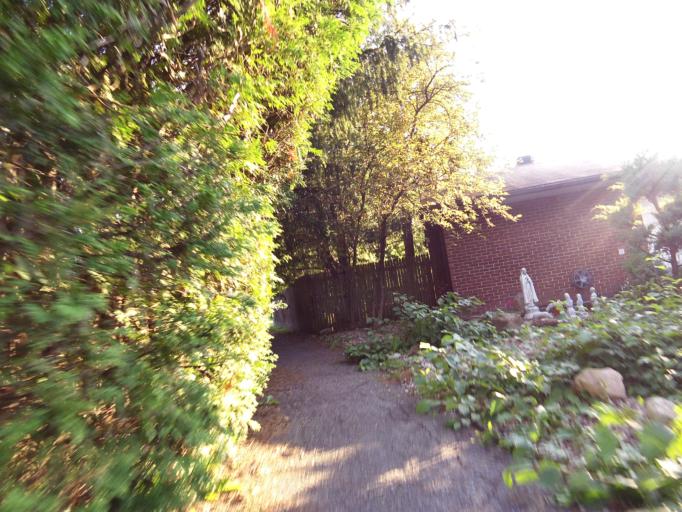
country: CA
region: Ontario
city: Bells Corners
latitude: 45.3268
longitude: -75.9032
